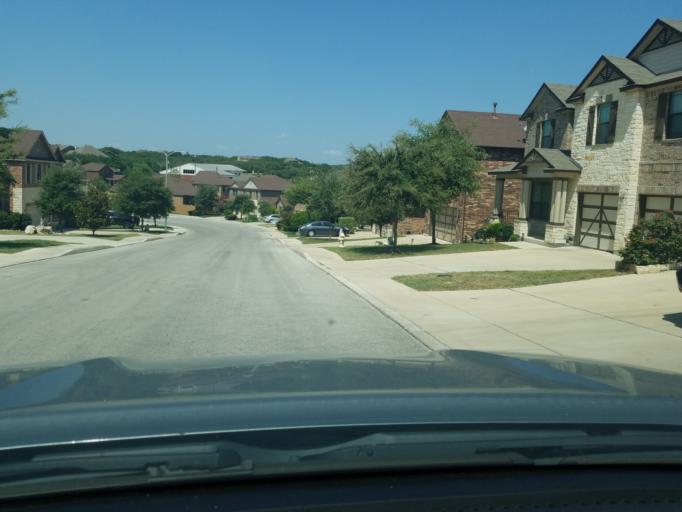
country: US
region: Texas
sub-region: Bexar County
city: Hollywood Park
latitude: 29.6395
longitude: -98.4738
